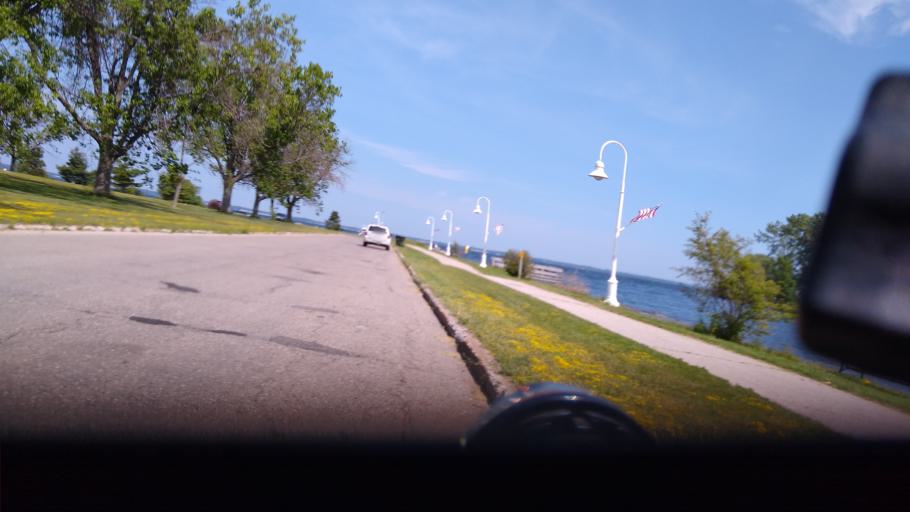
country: US
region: Michigan
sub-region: Delta County
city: Escanaba
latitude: 45.7432
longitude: -87.0396
